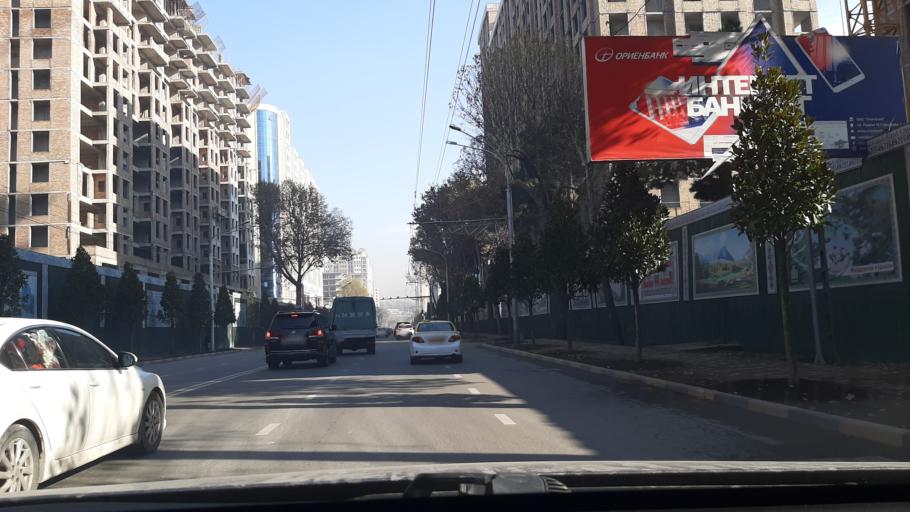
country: TJ
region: Dushanbe
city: Dushanbe
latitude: 38.5630
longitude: 68.8062
